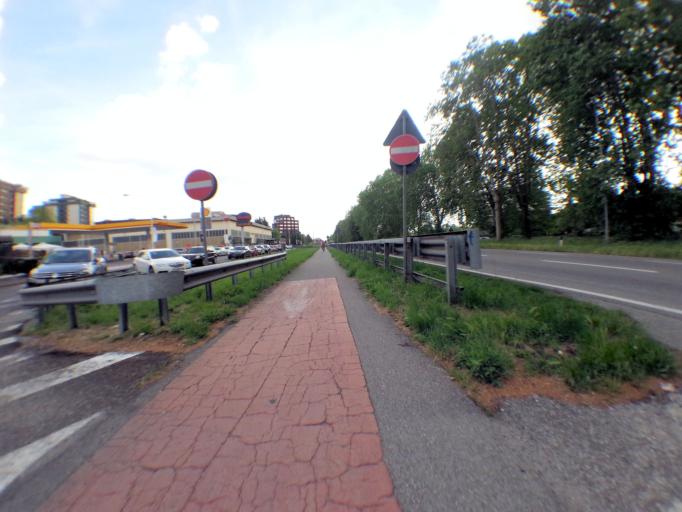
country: IT
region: Lombardy
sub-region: Citta metropolitana di Milano
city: Sesto San Giovanni
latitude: 45.5414
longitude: 9.2208
